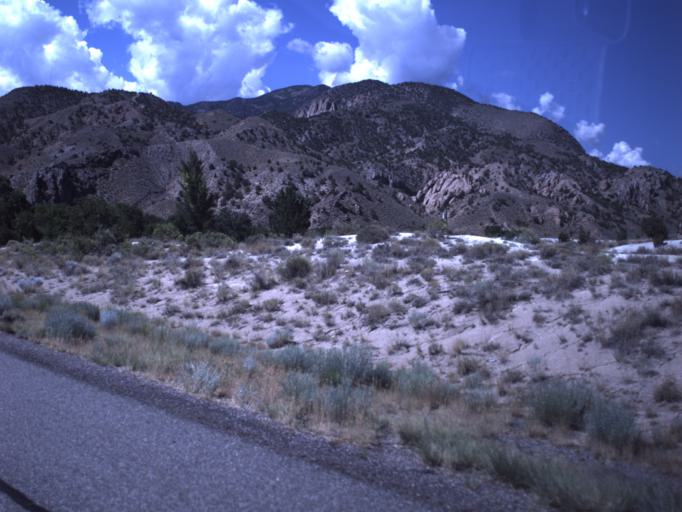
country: US
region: Utah
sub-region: Sevier County
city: Monroe
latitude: 38.5874
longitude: -112.2589
